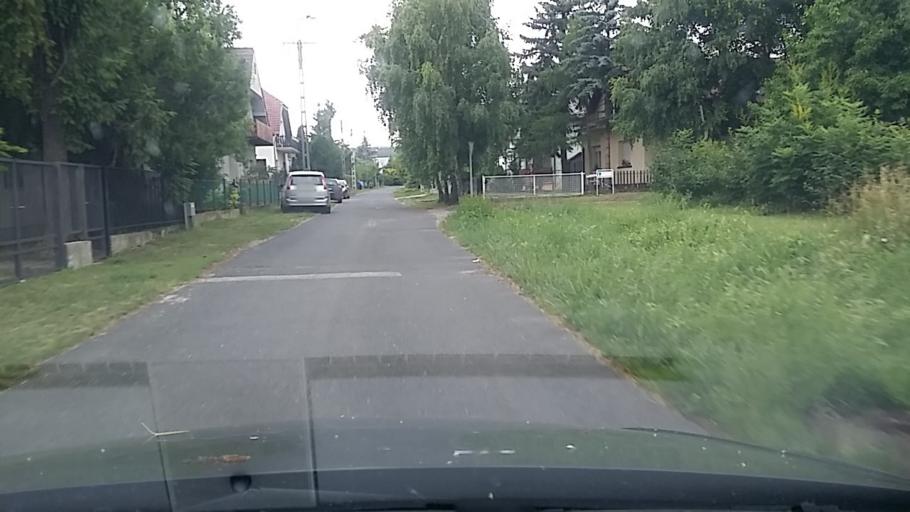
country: HU
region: Zala
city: Vonyarcvashegy
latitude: 46.7568
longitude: 17.3096
